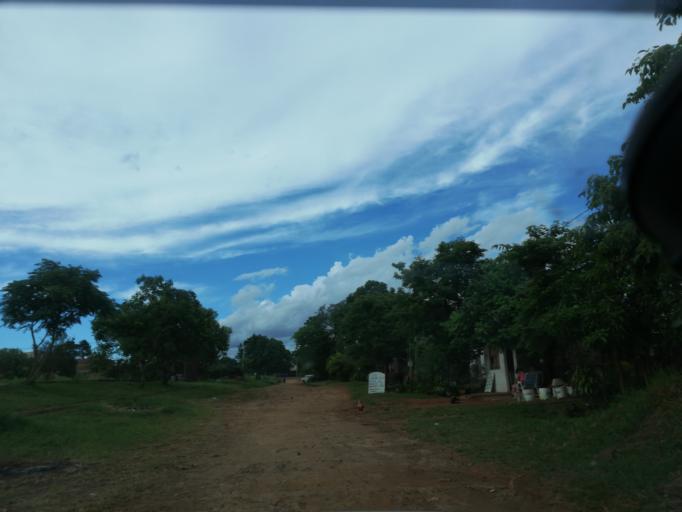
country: AR
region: Misiones
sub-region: Departamento de Capital
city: Posadas
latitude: -27.4214
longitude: -55.9224
